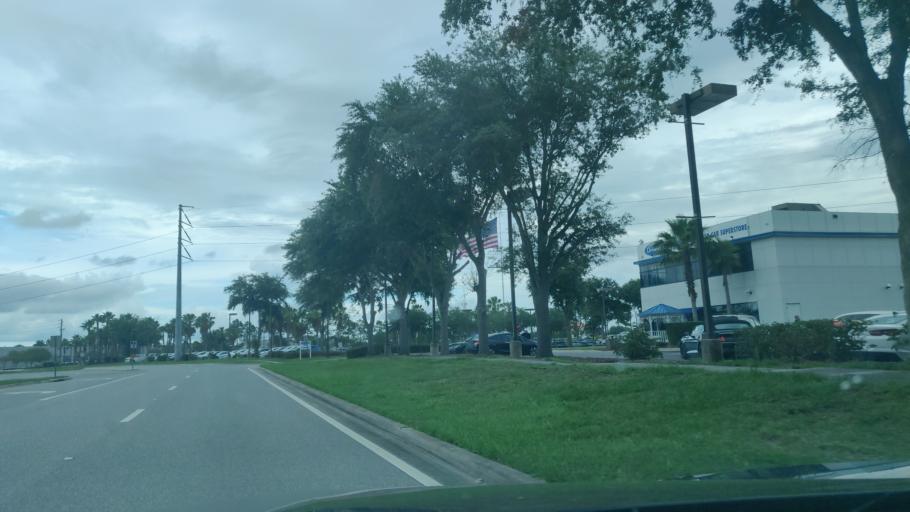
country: US
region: Florida
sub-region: Seminole County
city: Lake Mary
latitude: 28.8137
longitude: -81.3403
